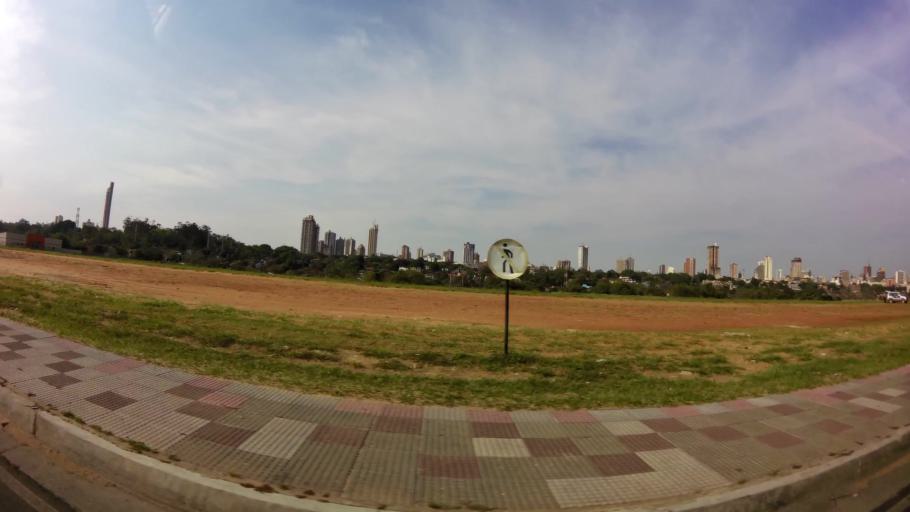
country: PY
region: Asuncion
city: Asuncion
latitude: -25.2765
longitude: -57.6245
